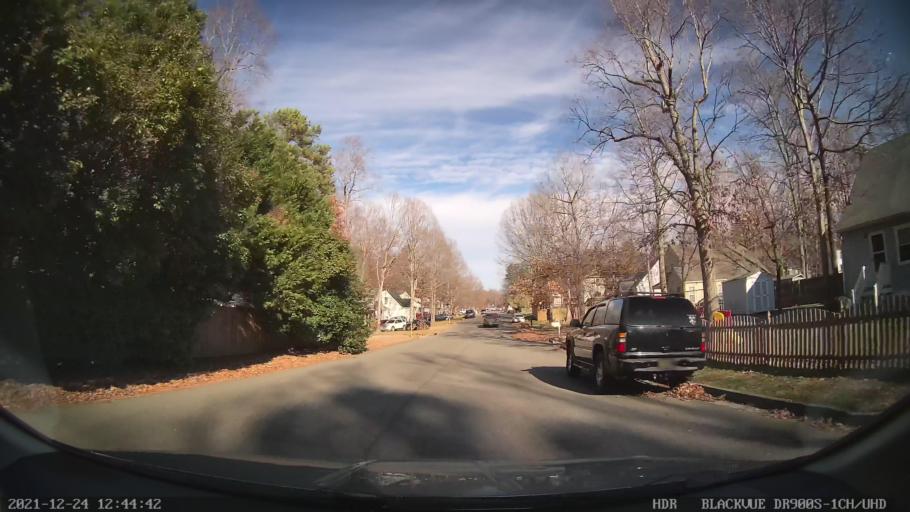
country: US
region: Virginia
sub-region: Henrico County
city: Short Pump
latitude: 37.6260
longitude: -77.6291
